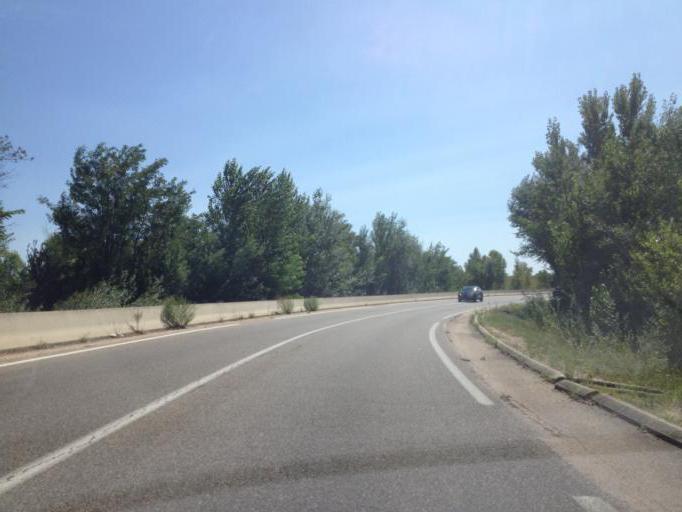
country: FR
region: Languedoc-Roussillon
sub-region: Departement du Gard
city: Roquemaure
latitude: 44.0564
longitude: 4.7820
